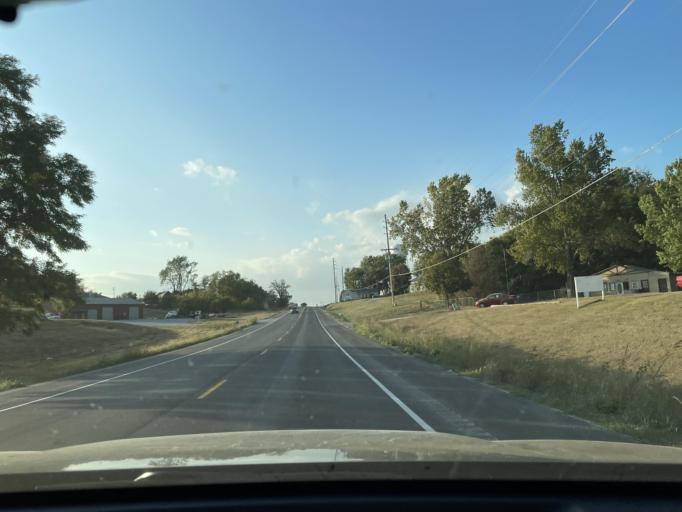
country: US
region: Missouri
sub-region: Andrew County
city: Country Club Village
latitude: 39.8272
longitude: -94.8567
